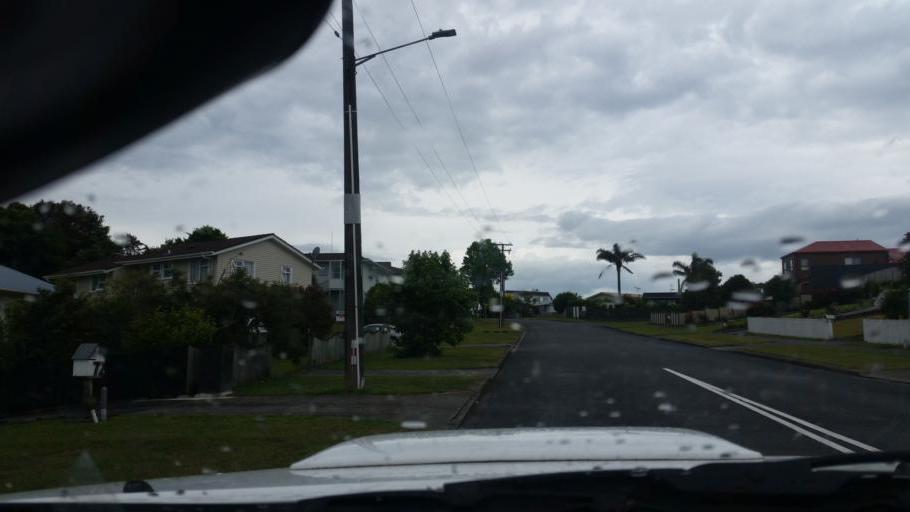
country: NZ
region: Northland
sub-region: Kaipara District
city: Dargaville
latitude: -35.9297
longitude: 173.8632
